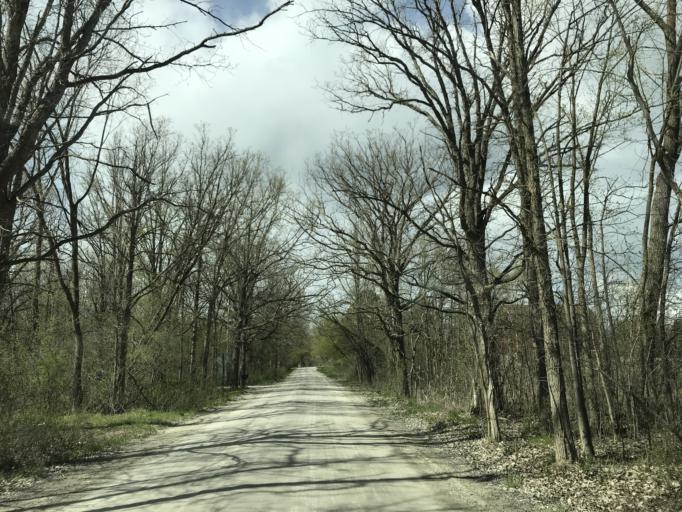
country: US
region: Michigan
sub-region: Livingston County
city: Whitmore Lake
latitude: 42.4055
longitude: -83.7237
